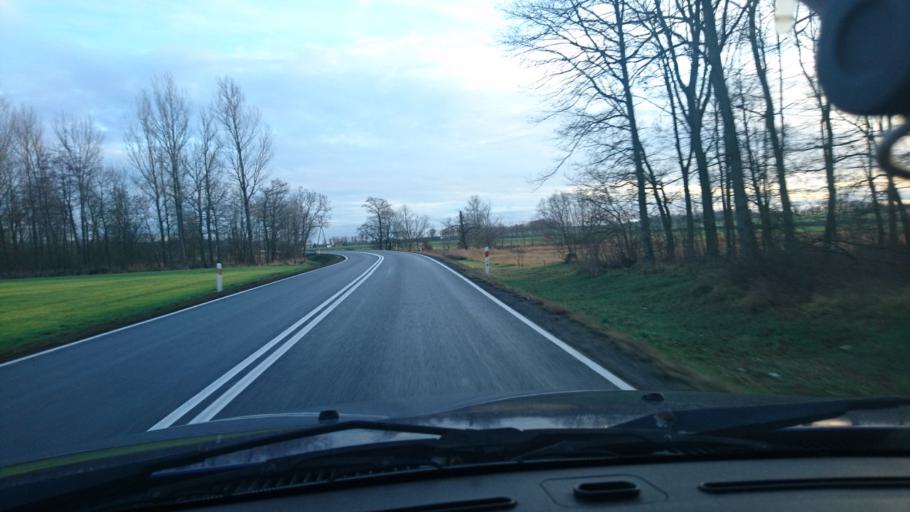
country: PL
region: Opole Voivodeship
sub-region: Powiat kluczborski
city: Byczyna
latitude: 51.1447
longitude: 18.1914
